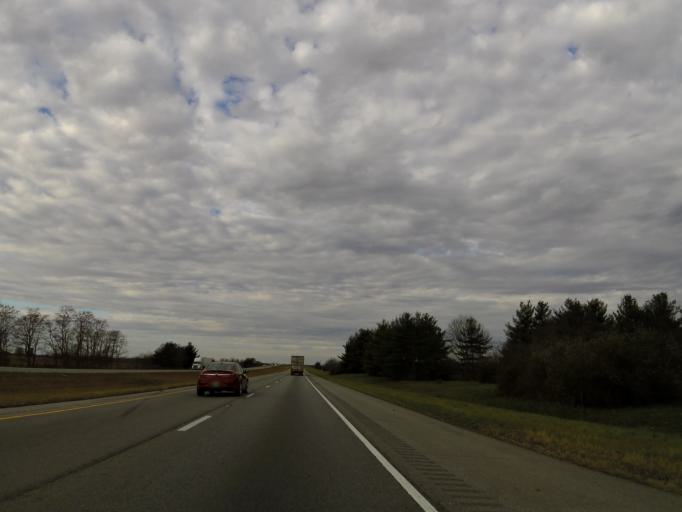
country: US
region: Illinois
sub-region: Jefferson County
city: Mount Vernon
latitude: 38.3622
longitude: -89.0612
